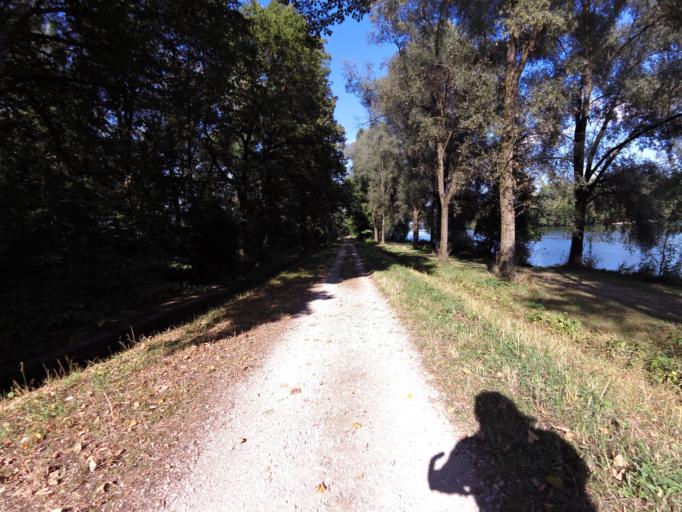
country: DE
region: Bavaria
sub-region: Lower Bavaria
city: Ergolding
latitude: 48.5596
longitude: 12.1811
